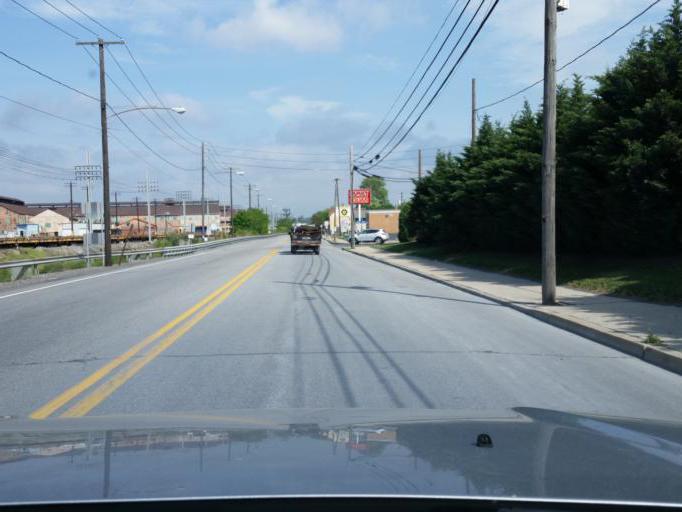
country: US
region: Pennsylvania
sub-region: Dauphin County
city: Enhaut
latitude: 40.2237
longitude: -76.8260
